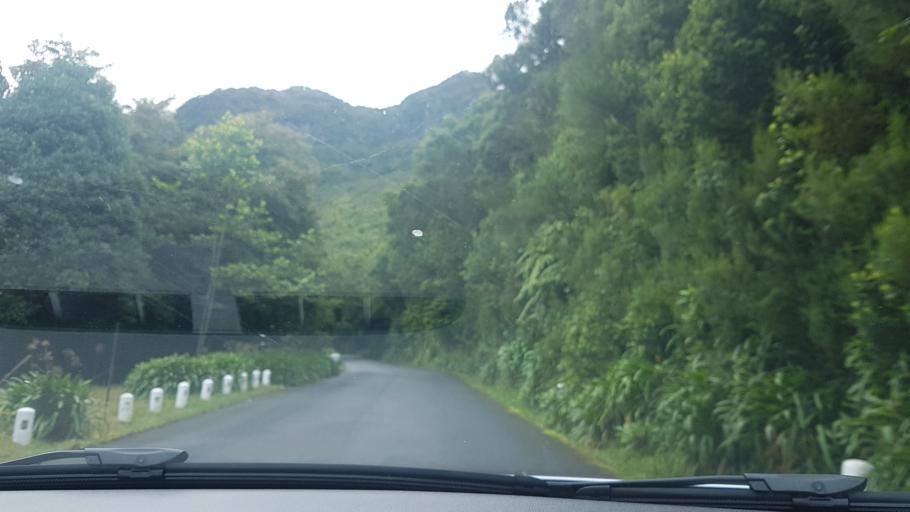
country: PT
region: Madeira
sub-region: Sao Vicente
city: Sao Vicente
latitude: 32.7558
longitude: -17.0177
